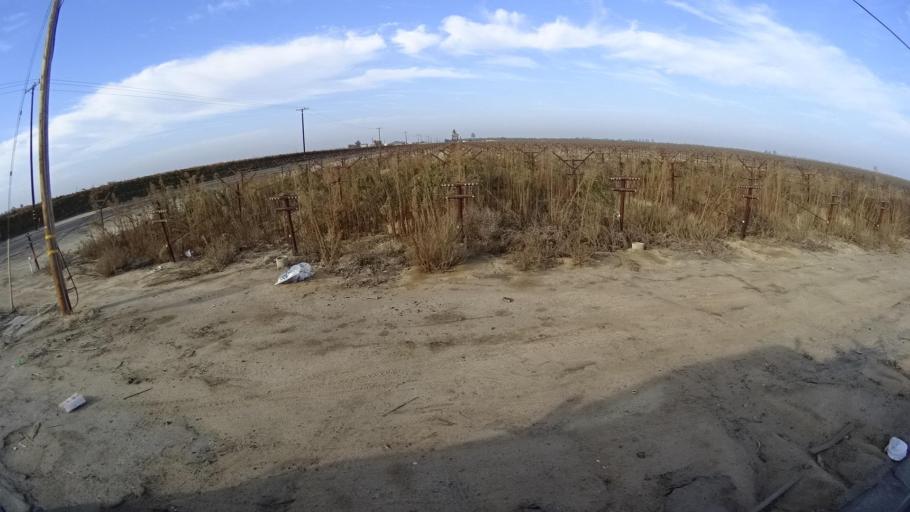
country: US
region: California
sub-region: Kern County
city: Delano
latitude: 35.7471
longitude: -119.2053
